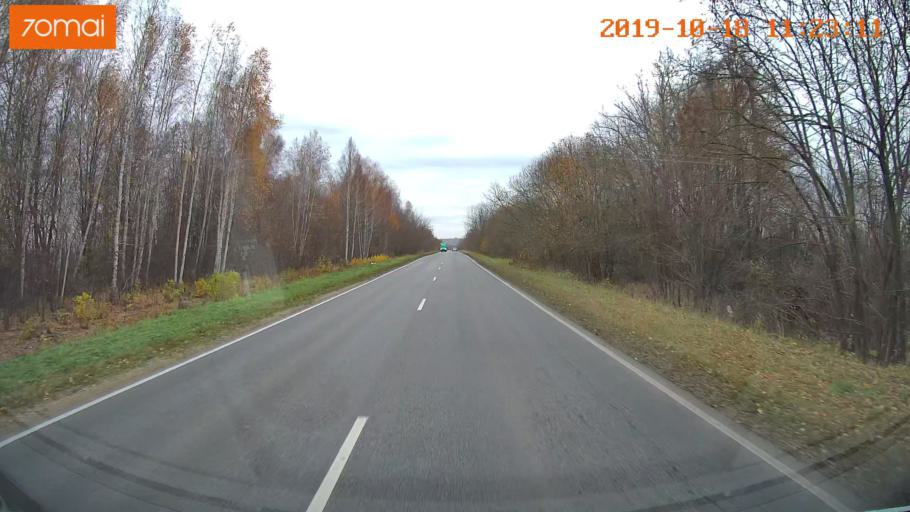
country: RU
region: Tula
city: Kimovsk
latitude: 54.0979
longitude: 38.5907
